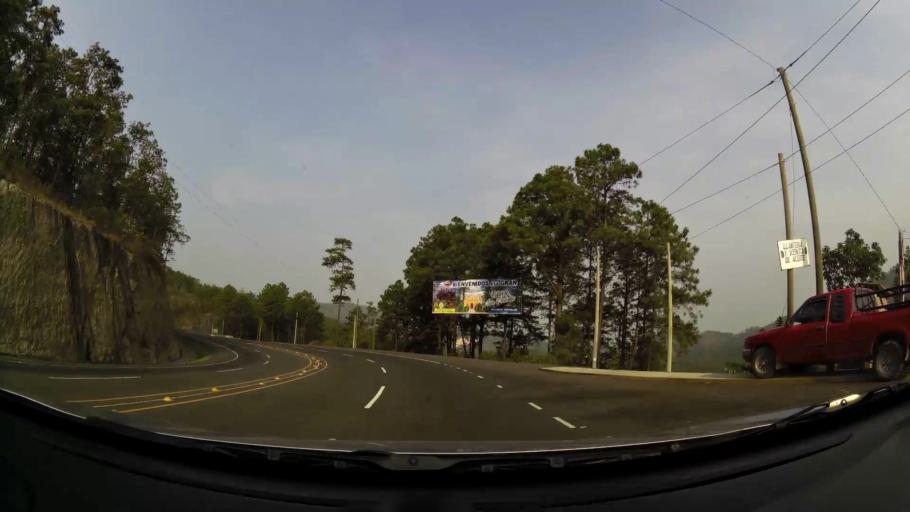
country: HN
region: Francisco Morazan
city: Zambrano
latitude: 14.2858
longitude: -87.4600
